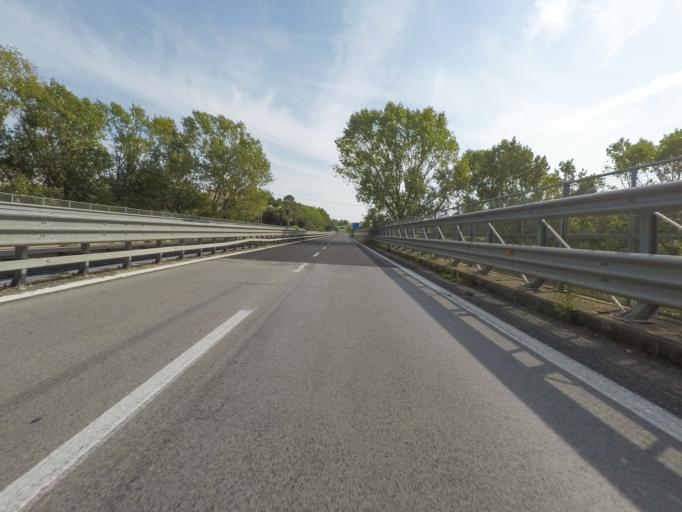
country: IT
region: Latium
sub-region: Provincia di Viterbo
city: Montalto di Castro
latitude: 42.3523
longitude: 11.5981
